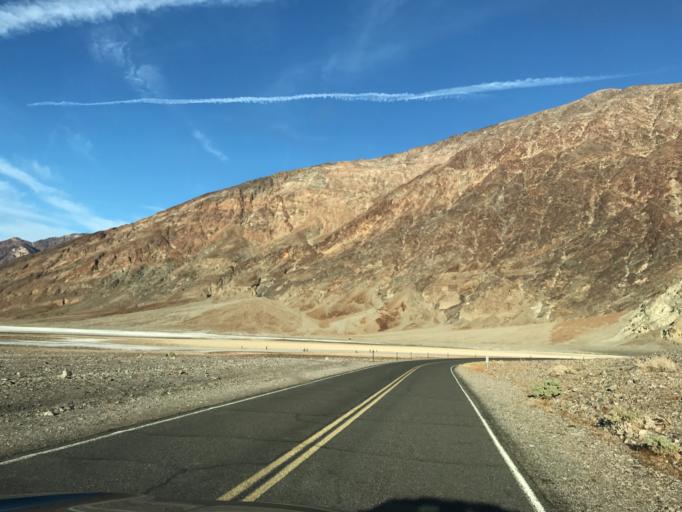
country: US
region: Nevada
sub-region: Nye County
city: Beatty
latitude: 36.2285
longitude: -116.7743
